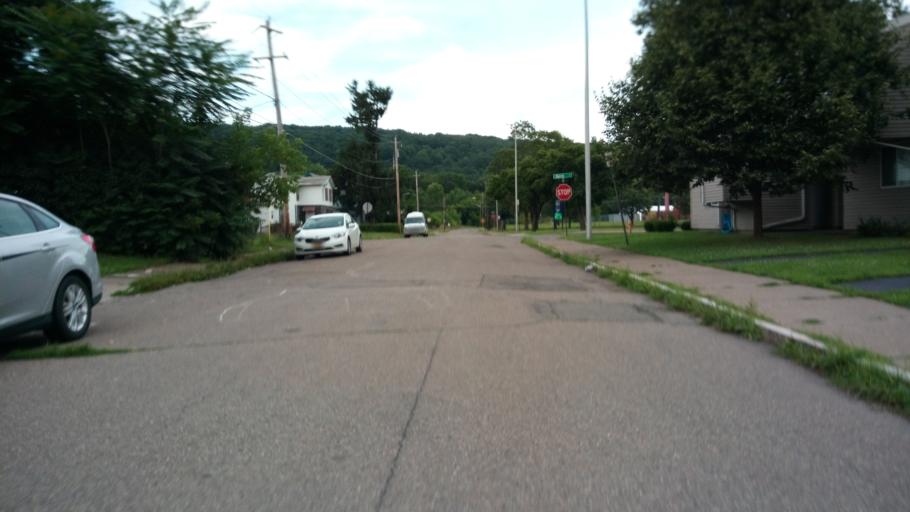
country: US
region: New York
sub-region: Chemung County
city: Elmira
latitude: 42.0928
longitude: -76.7923
